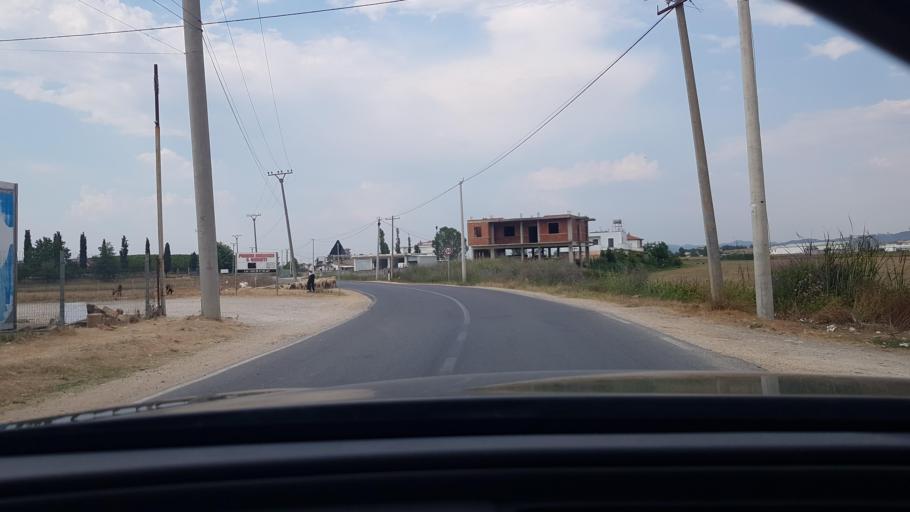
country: AL
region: Durres
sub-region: Rrethi i Durresit
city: Katundi i Ri
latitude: 41.4123
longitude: 19.5470
